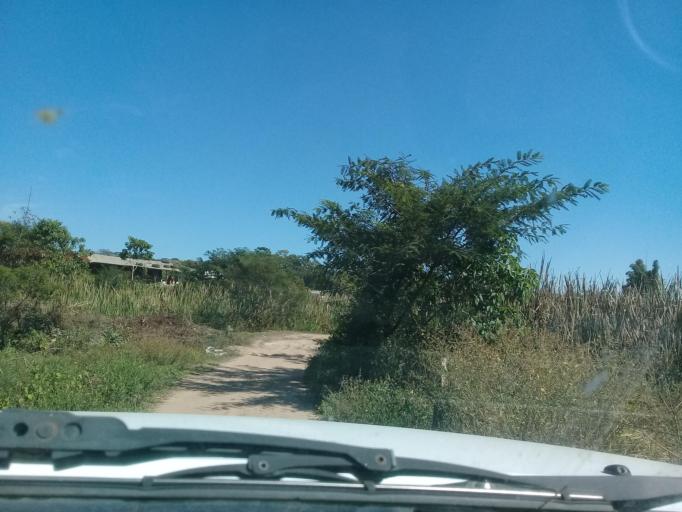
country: MX
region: Veracruz
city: El Castillo
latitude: 19.5494
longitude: -96.8557
